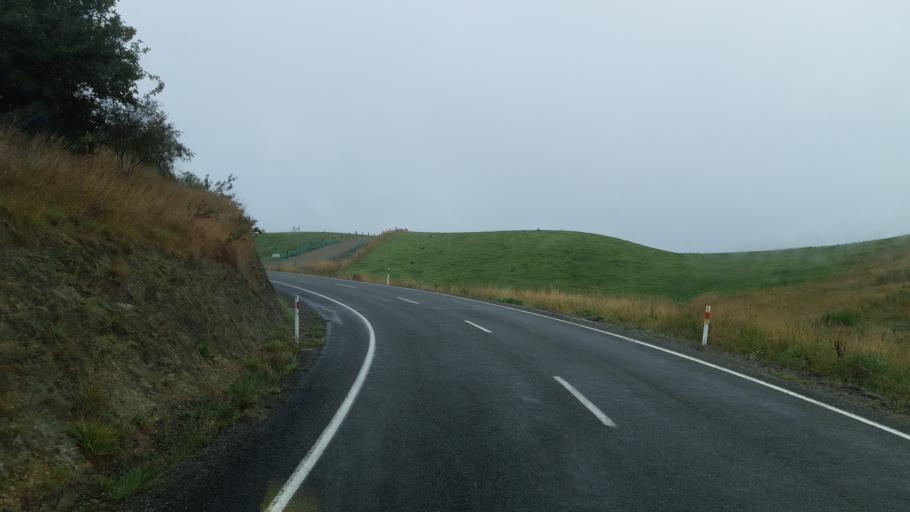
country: NZ
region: Otago
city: Oamaru
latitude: -44.9128
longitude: 170.8374
